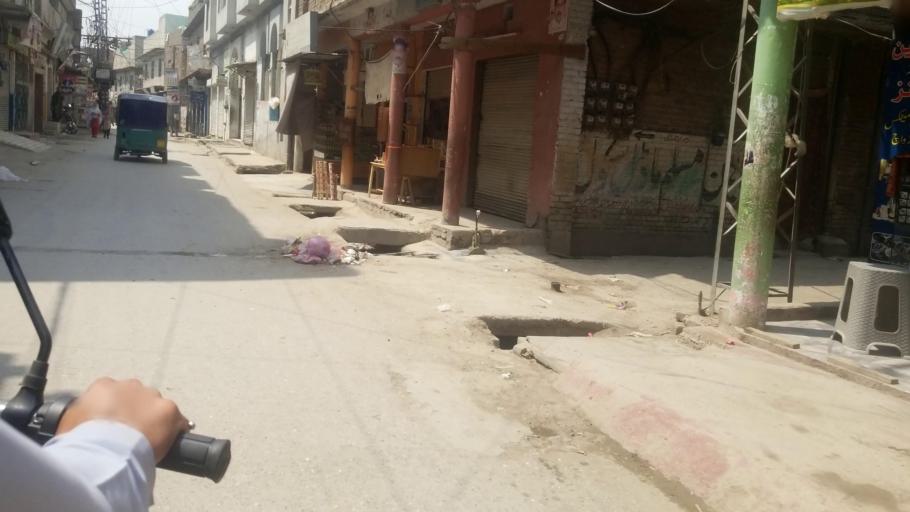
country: PK
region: Khyber Pakhtunkhwa
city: Peshawar
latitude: 34.0287
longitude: 71.5838
